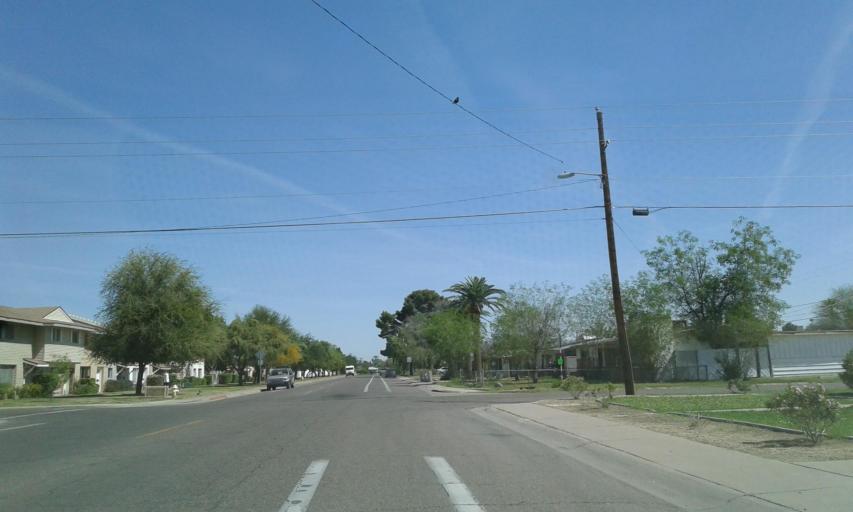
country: US
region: Arizona
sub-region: Maricopa County
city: Phoenix
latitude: 33.5023
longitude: -112.0961
